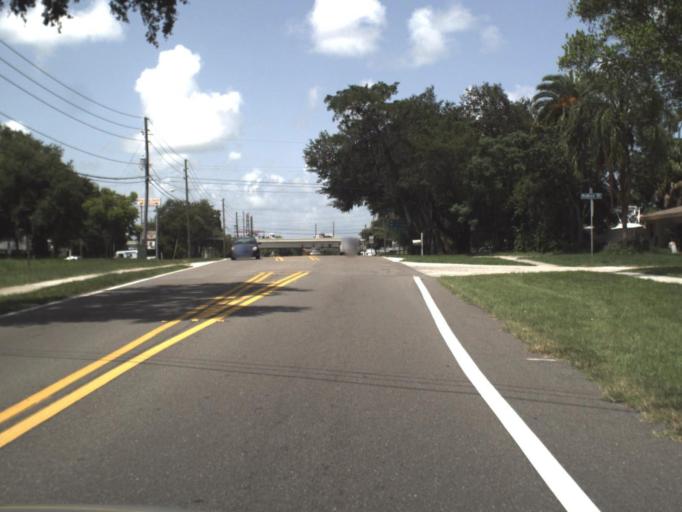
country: US
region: Florida
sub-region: Pinellas County
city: Safety Harbor
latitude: 27.9827
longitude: -82.7263
